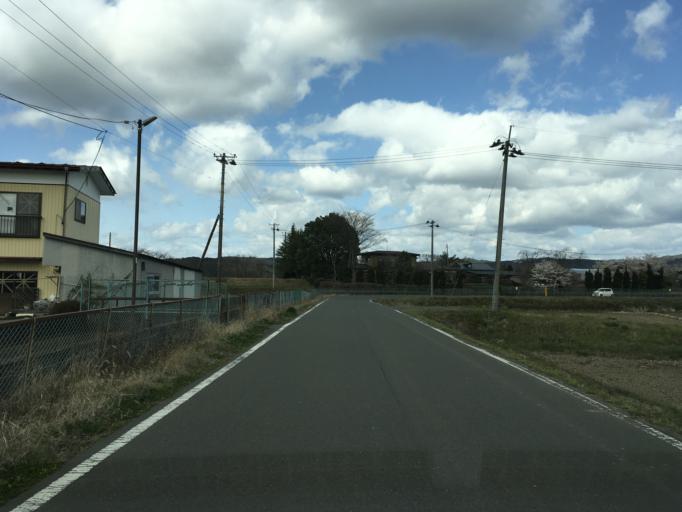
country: JP
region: Iwate
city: Ichinoseki
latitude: 38.7478
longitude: 141.2570
